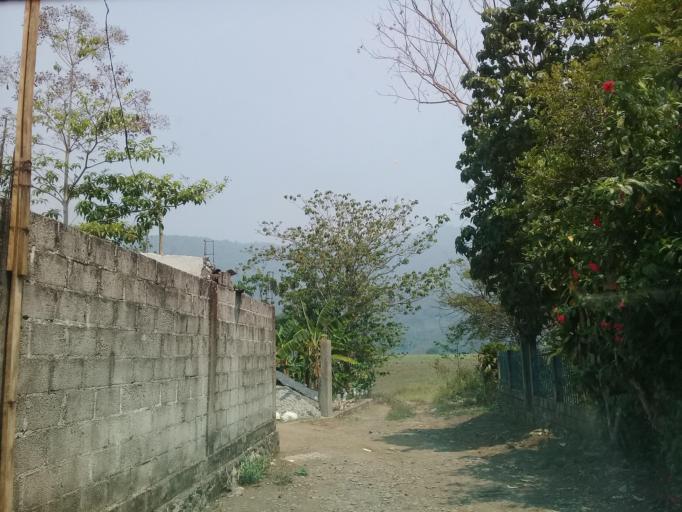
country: MX
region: Veracruz
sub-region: Tezonapa
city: Laguna Chica (Pueblo Nuevo)
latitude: 18.5575
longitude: -96.7267
